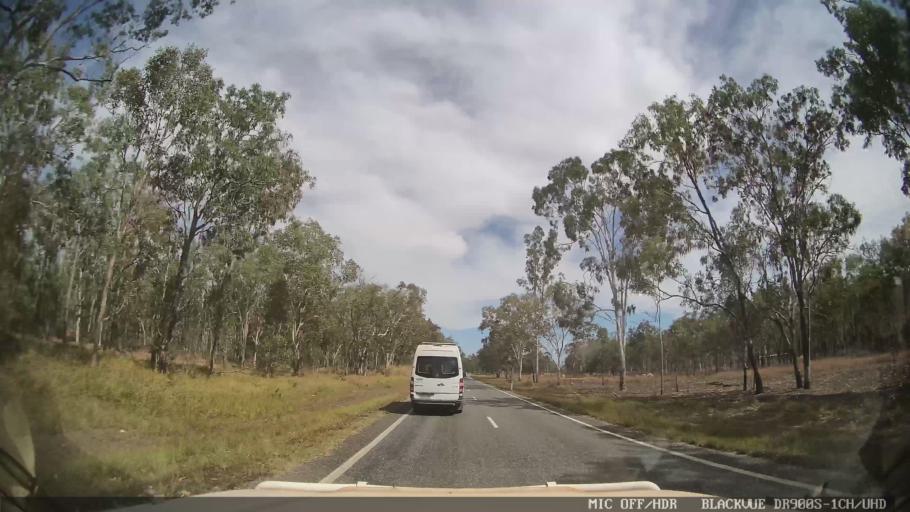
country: AU
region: Queensland
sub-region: Cairns
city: Port Douglas
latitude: -16.7265
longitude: 145.3525
